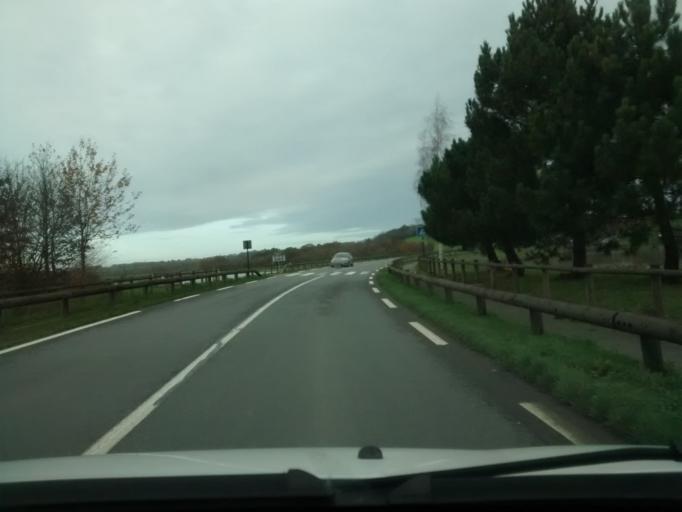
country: FR
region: Brittany
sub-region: Departement d'Ille-et-Vilaine
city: Montreuil-sous-Perouse
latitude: 48.1428
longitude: -1.2513
